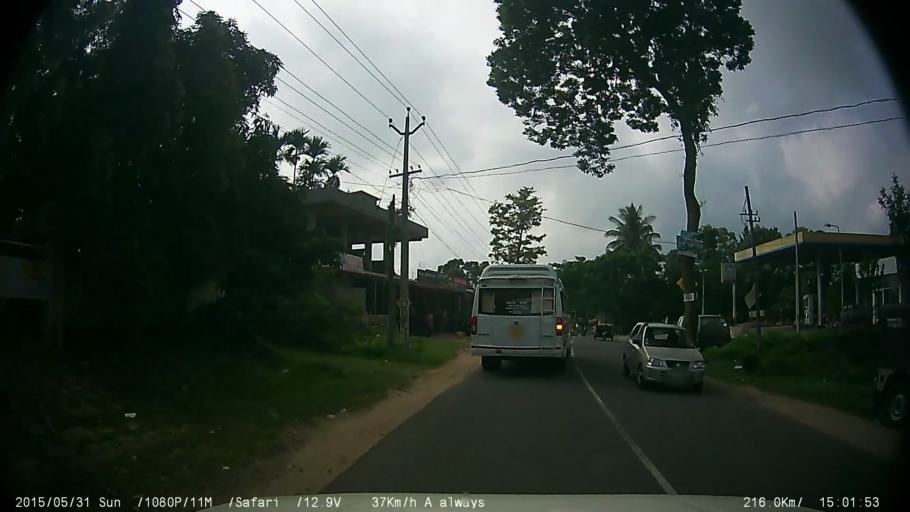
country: IN
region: Kerala
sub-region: Wayanad
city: Kalpetta
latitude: 11.6256
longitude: 76.2103
